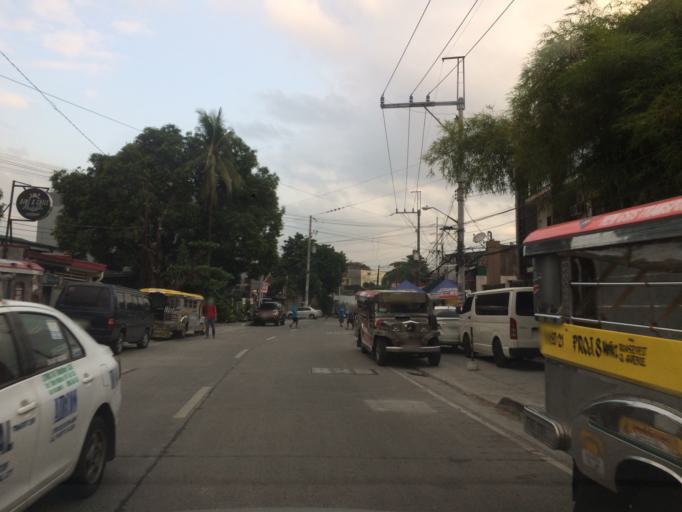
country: PH
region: Calabarzon
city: Bagong Pagasa
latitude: 14.6772
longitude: 121.0258
